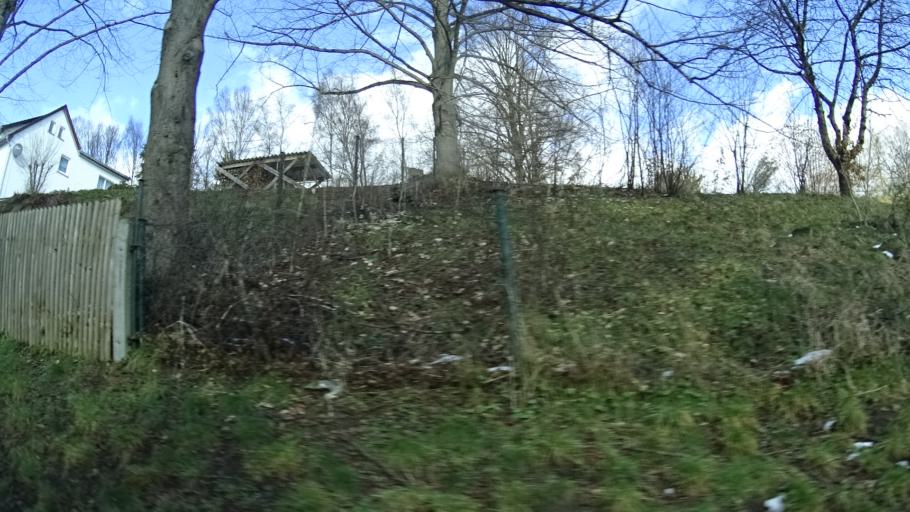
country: DE
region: Thuringia
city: Suhl
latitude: 50.6117
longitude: 10.6770
